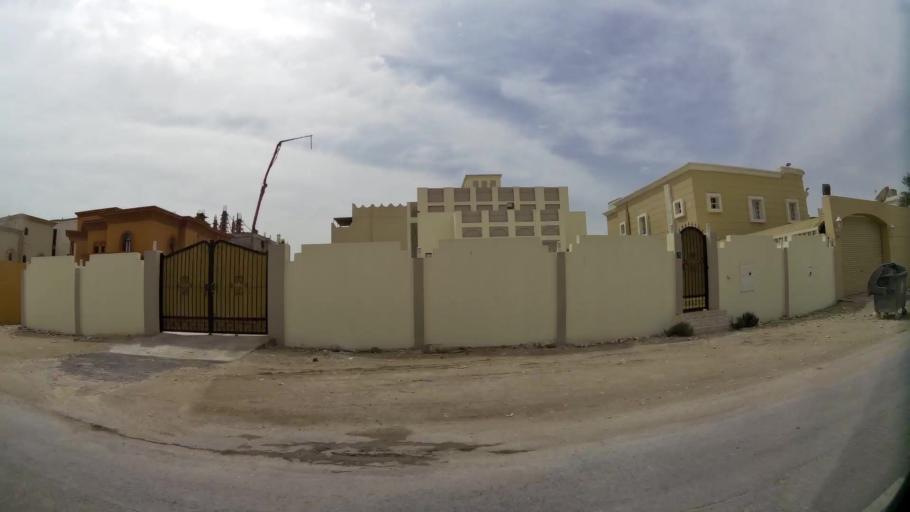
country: QA
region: Al Wakrah
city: Al Wukayr
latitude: 25.2020
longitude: 51.4633
